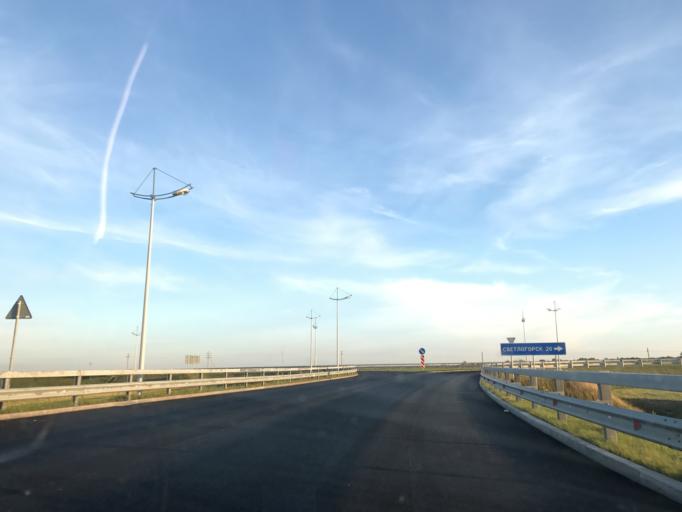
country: RU
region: Kaliningrad
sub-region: Zelenogradskiy Rayon
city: Zelenogradsk
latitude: 54.9233
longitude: 20.4054
